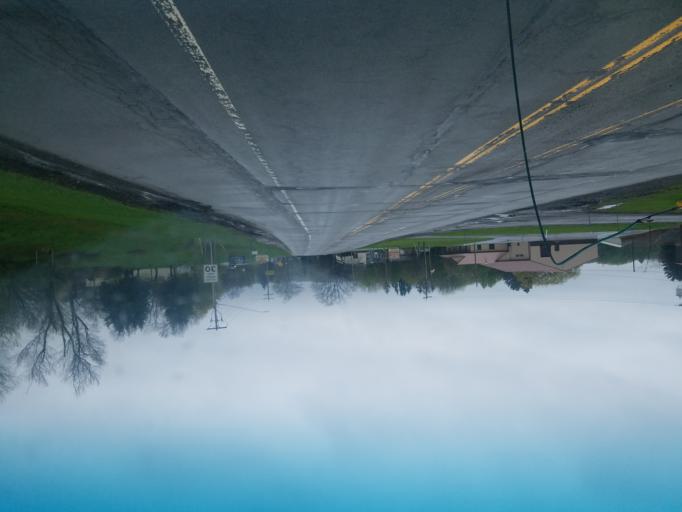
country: US
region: New York
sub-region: Chautauqua County
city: Mayville
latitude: 42.1544
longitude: -79.5939
